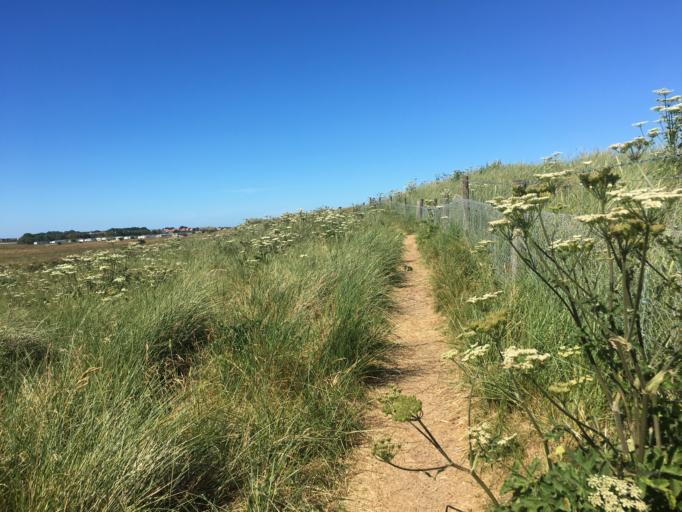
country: GB
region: England
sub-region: Northumberland
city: Beadnell
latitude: 55.5411
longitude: -1.6389
